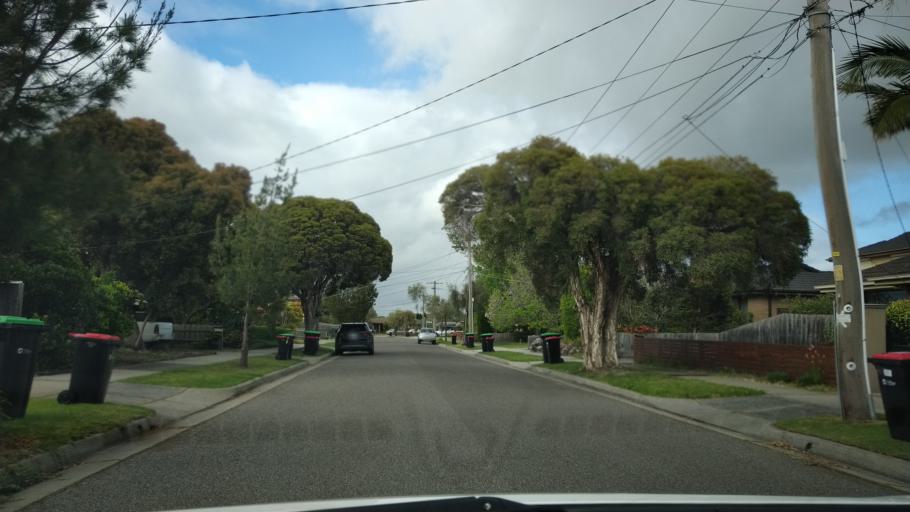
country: AU
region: Victoria
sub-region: Greater Dandenong
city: Keysborough
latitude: -37.9886
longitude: 145.1778
